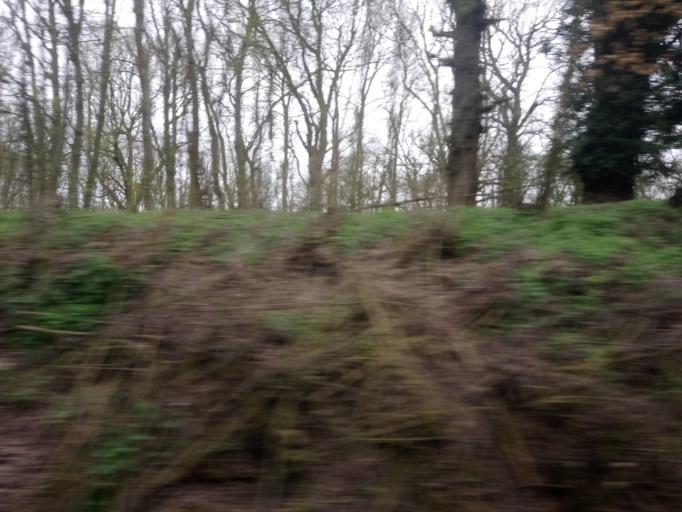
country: GB
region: England
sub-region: Suffolk
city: Ipswich
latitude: 52.0291
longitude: 1.1384
